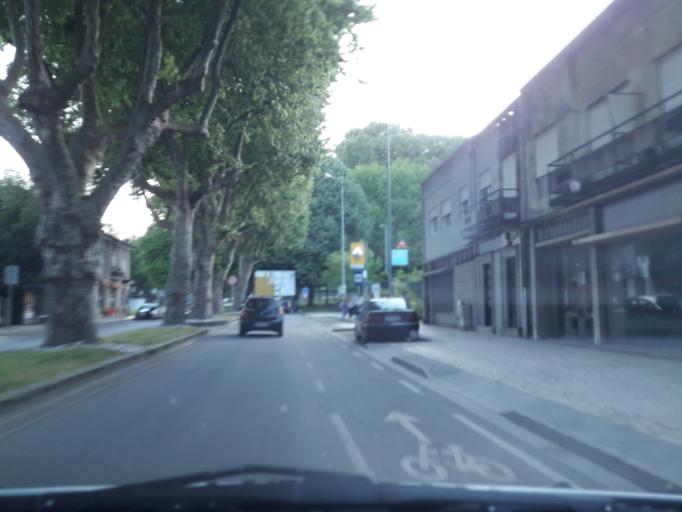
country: PT
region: Braga
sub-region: Vila Nova de Famalicao
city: Vila Nova de Famalicao
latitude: 41.4076
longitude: -8.5227
